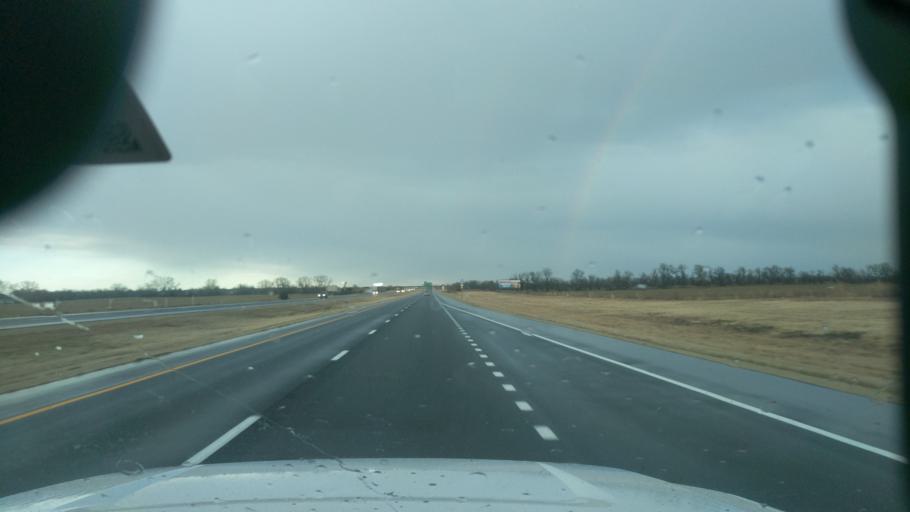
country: US
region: Kansas
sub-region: Harvey County
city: Newton
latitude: 38.0029
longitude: -97.3279
